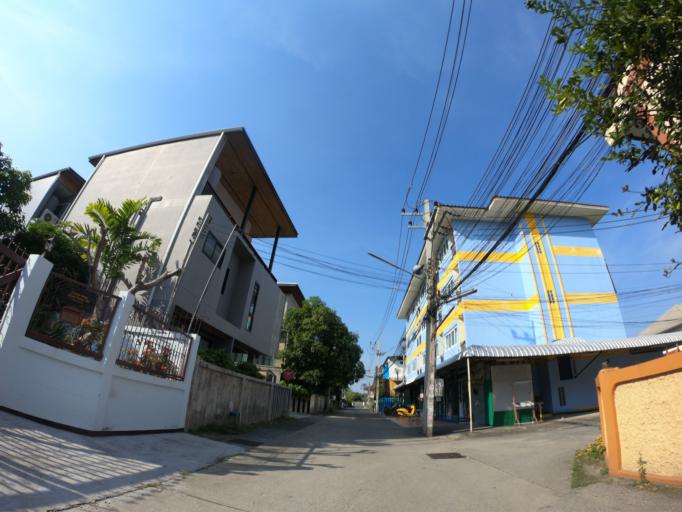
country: TH
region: Chiang Mai
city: Chiang Mai
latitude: 18.8170
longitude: 98.9868
